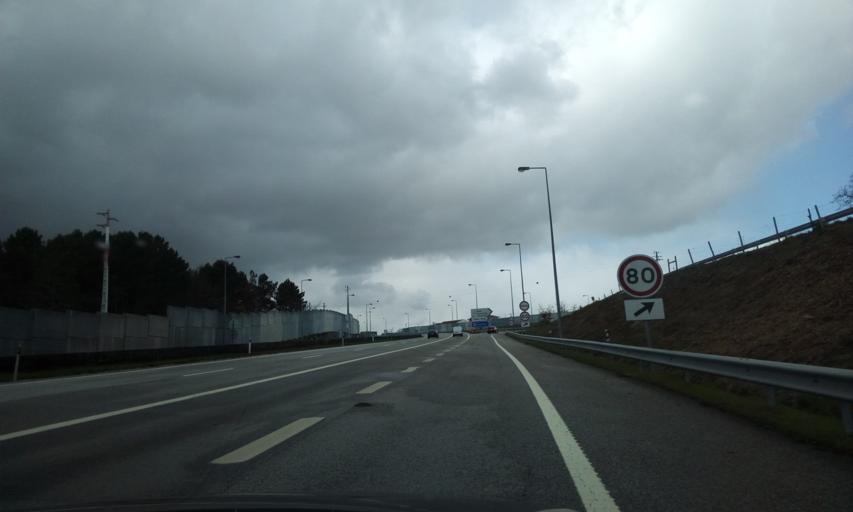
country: PT
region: Viseu
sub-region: Viseu
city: Rio de Loba
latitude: 40.6361
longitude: -7.8475
